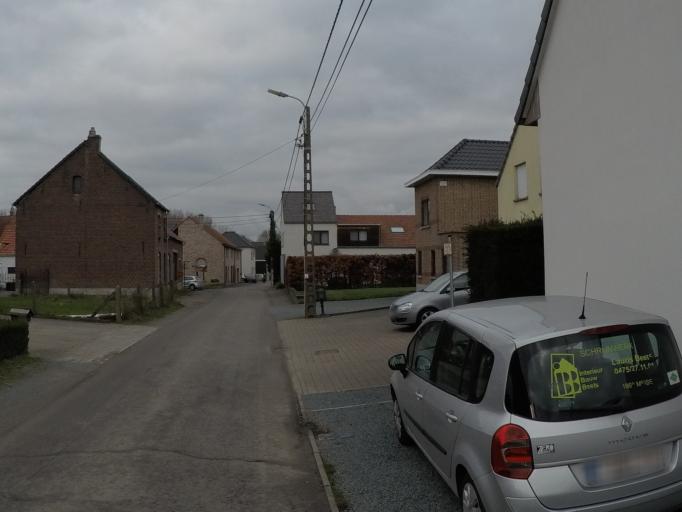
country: BE
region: Flanders
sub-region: Provincie Vlaams-Brabant
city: Merchtem
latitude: 50.9943
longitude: 4.2447
